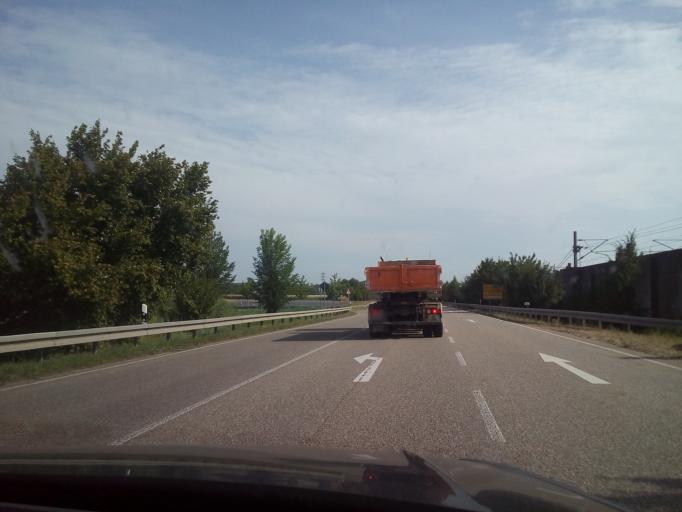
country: DE
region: Baden-Wuerttemberg
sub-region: Karlsruhe Region
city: Rastatt
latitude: 48.8129
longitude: 8.2092
